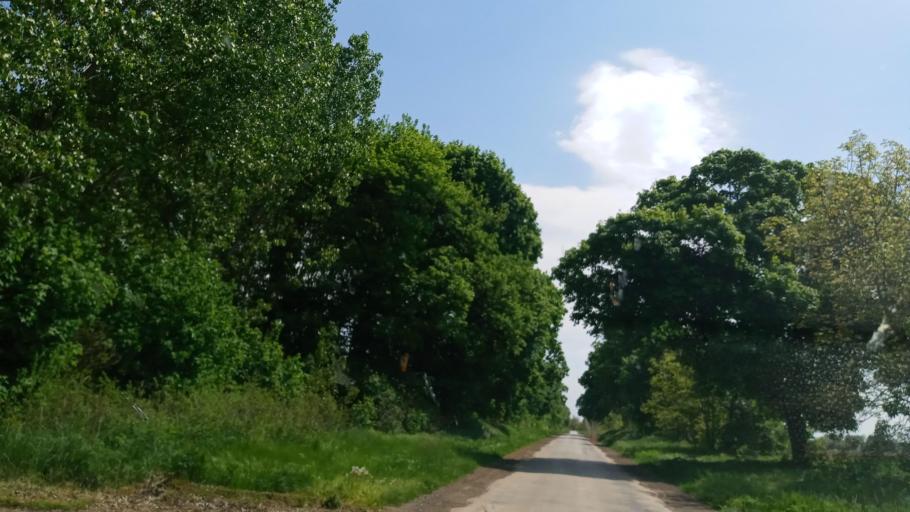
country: HU
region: Baranya
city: Villany
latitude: 45.8270
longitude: 18.5029
